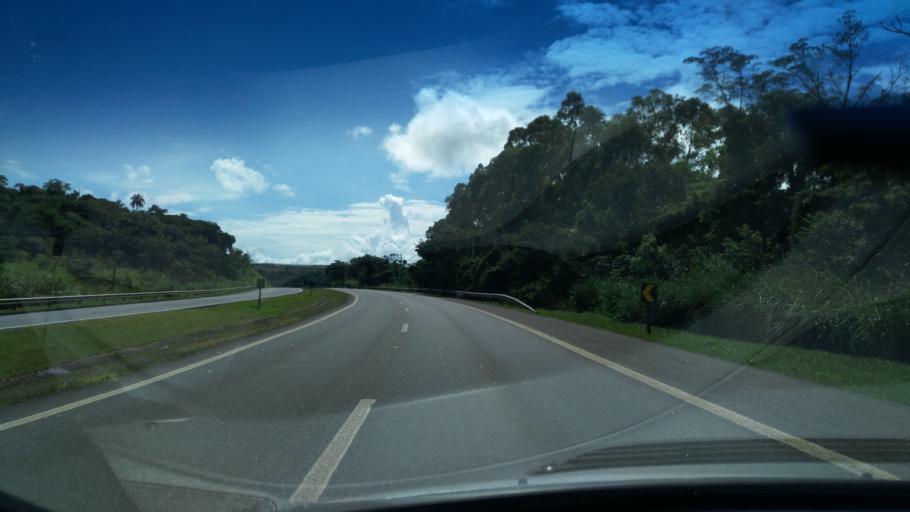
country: BR
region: Sao Paulo
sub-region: Santo Antonio Do Jardim
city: Espirito Santo do Pinhal
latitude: -22.2179
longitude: -46.7862
